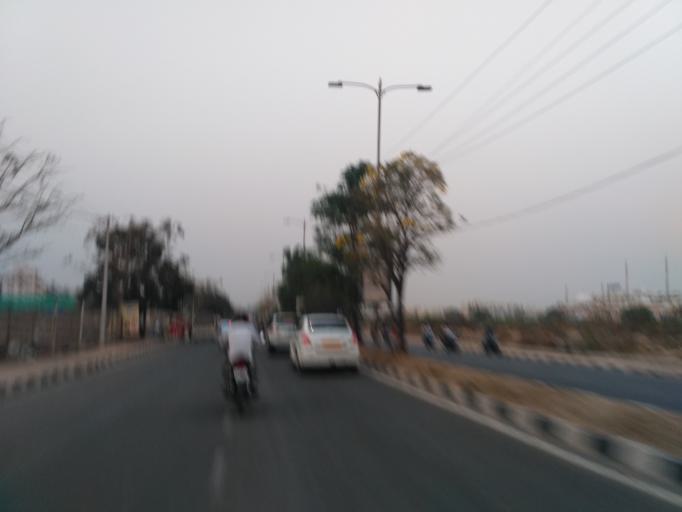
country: IN
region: Telangana
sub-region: Rangareddi
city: Kukatpalli
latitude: 17.4454
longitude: 78.3944
